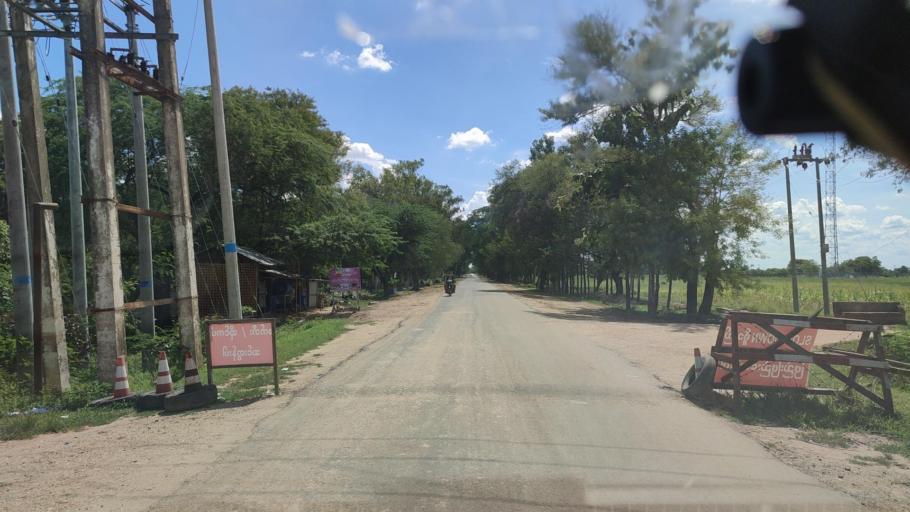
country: MM
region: Magway
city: Taungdwingyi
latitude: 19.9988
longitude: 95.5223
